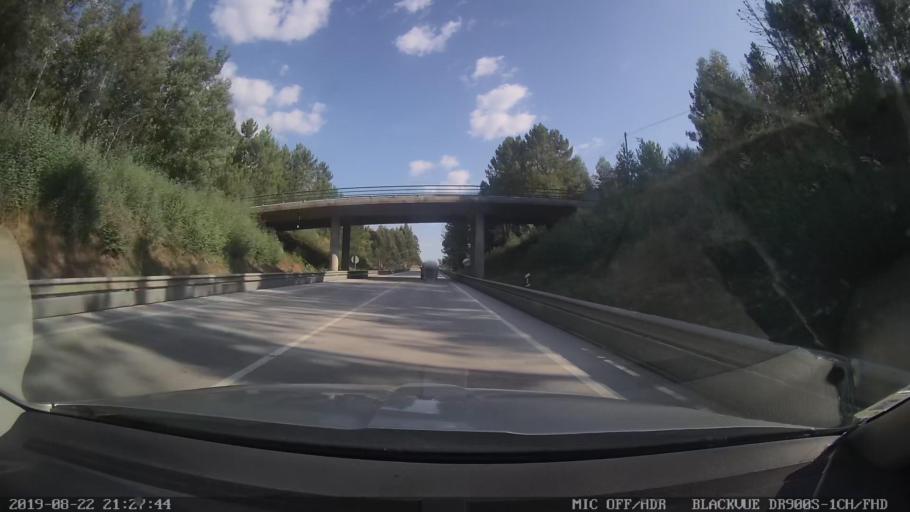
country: PT
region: Leiria
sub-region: Pedrogao Grande
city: Pedrogao Grande
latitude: 39.8828
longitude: -8.1200
